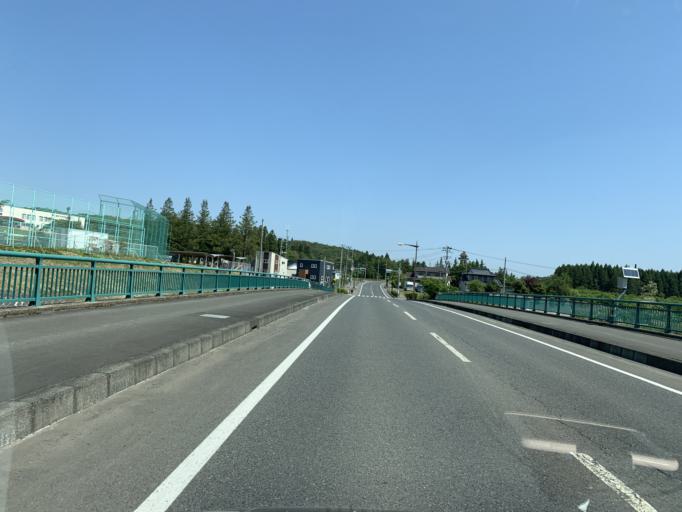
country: JP
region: Iwate
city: Kitakami
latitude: 39.2056
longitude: 141.0948
